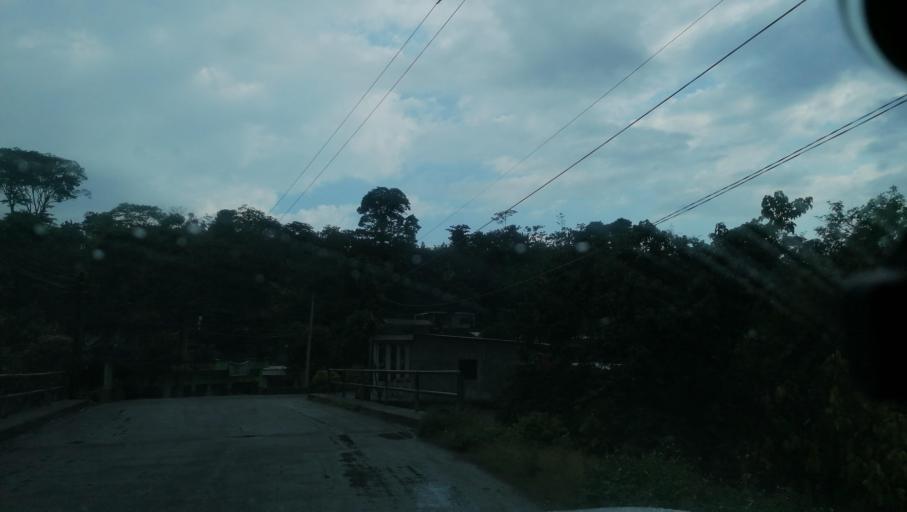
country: MX
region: Chiapas
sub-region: Cacahoatan
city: Benito Juarez
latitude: 15.0499
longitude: -92.1892
